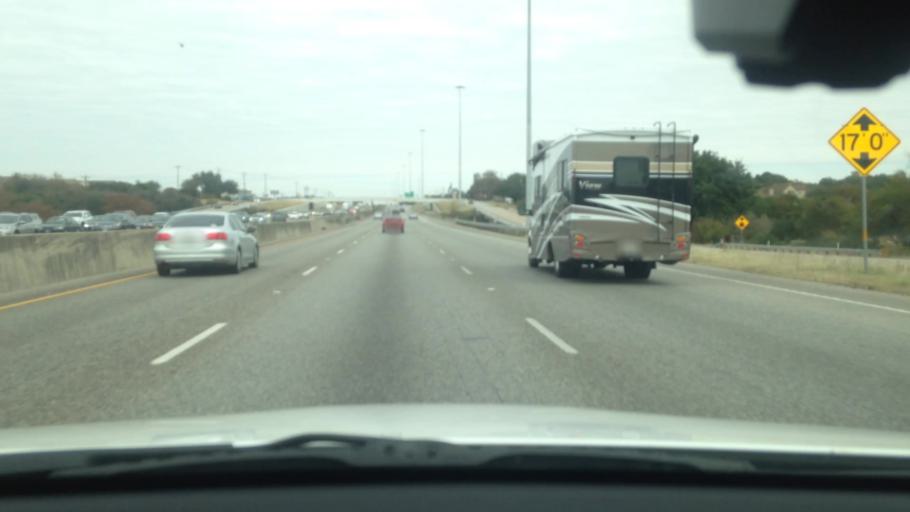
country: US
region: Texas
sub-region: Travis County
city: Onion Creek
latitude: 30.1329
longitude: -97.7987
